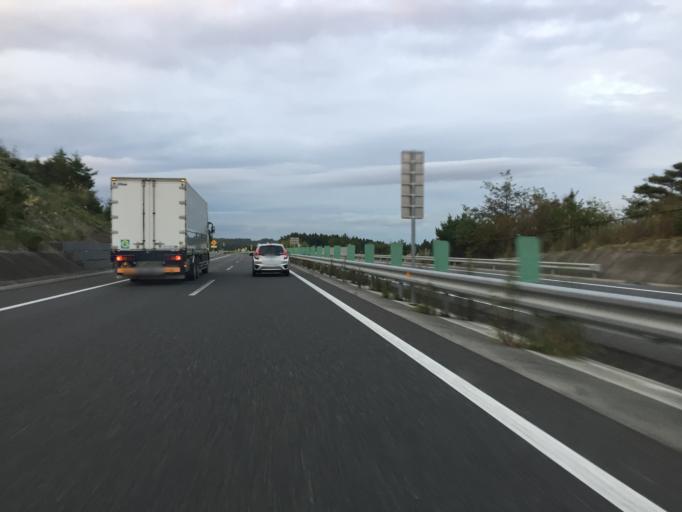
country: JP
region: Miyagi
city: Marumori
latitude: 37.7651
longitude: 140.9016
